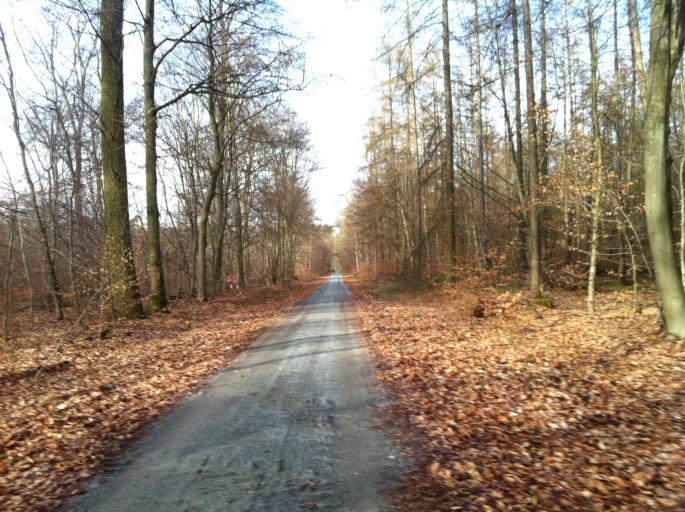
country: DE
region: Hesse
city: Langen
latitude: 50.0259
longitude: 8.6290
